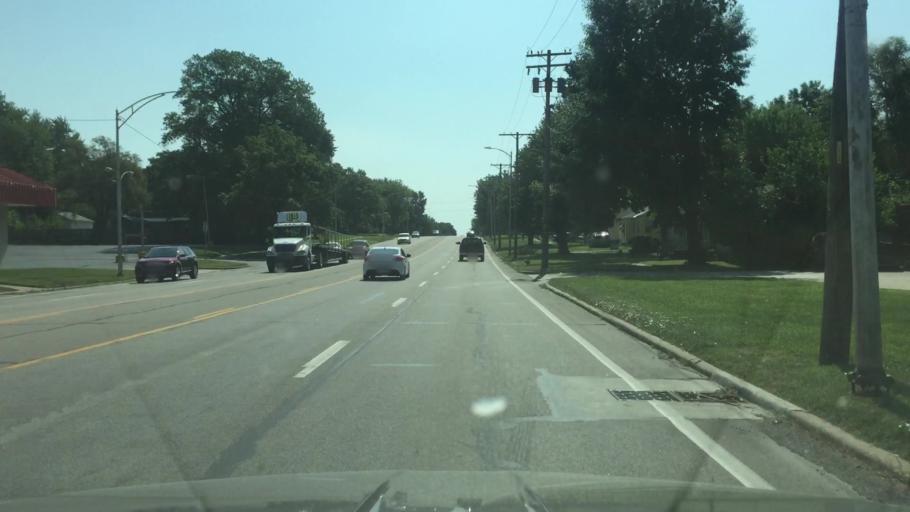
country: US
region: Missouri
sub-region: Pettis County
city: Sedalia
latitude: 38.7033
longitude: -93.2063
